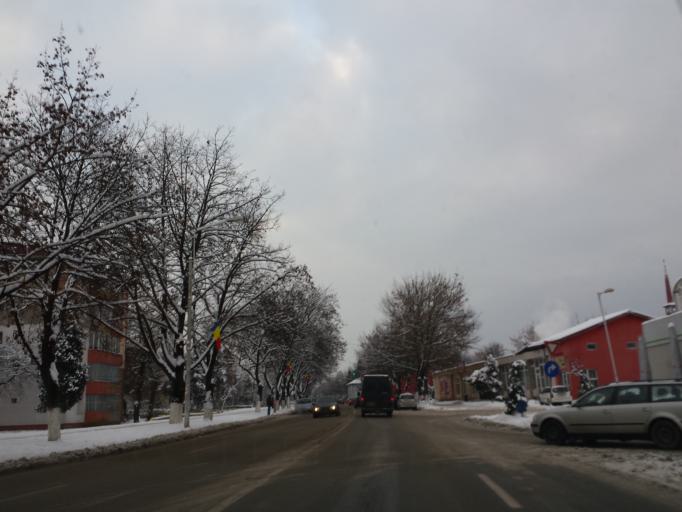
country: RO
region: Hunedoara
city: Hunedoara
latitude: 45.7624
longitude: 22.9025
